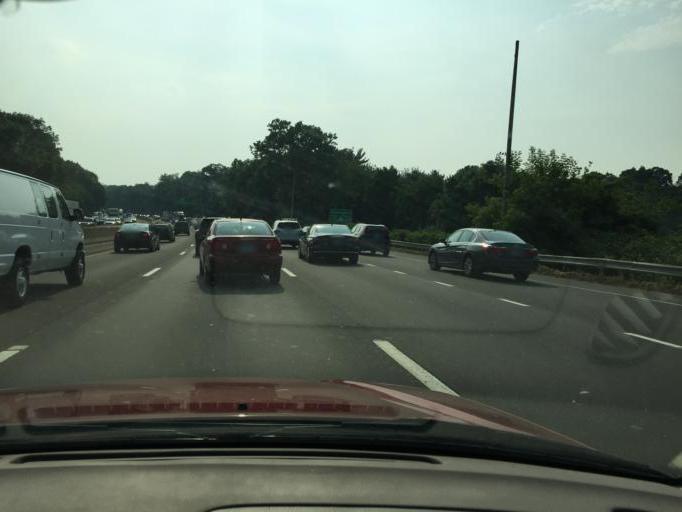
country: US
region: Connecticut
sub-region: Fairfield County
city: Riverside
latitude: 41.0451
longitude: -73.5638
